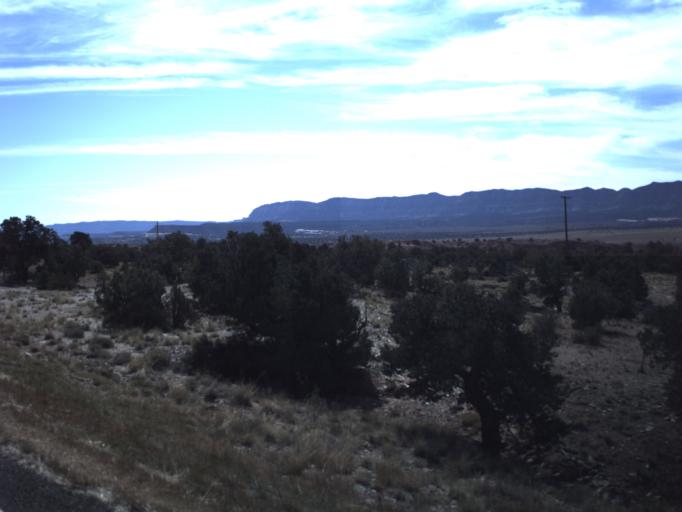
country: US
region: Utah
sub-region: Wayne County
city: Loa
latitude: 37.7352
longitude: -111.5431
